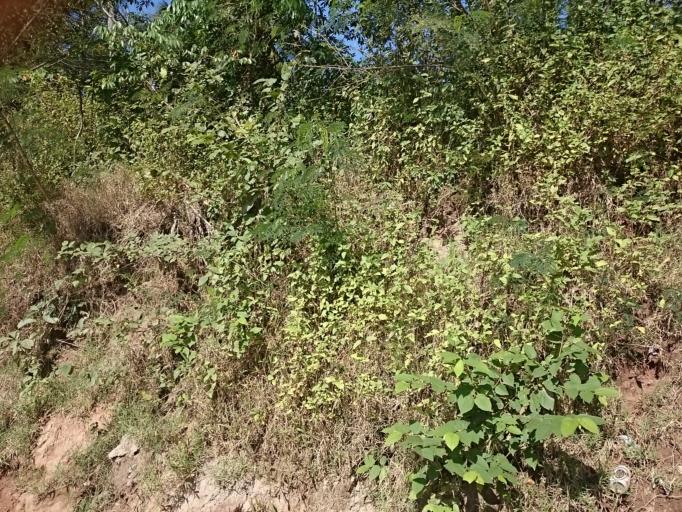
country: PE
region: San Martin
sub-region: Picota
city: Pilluana
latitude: -6.7387
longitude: -76.2900
